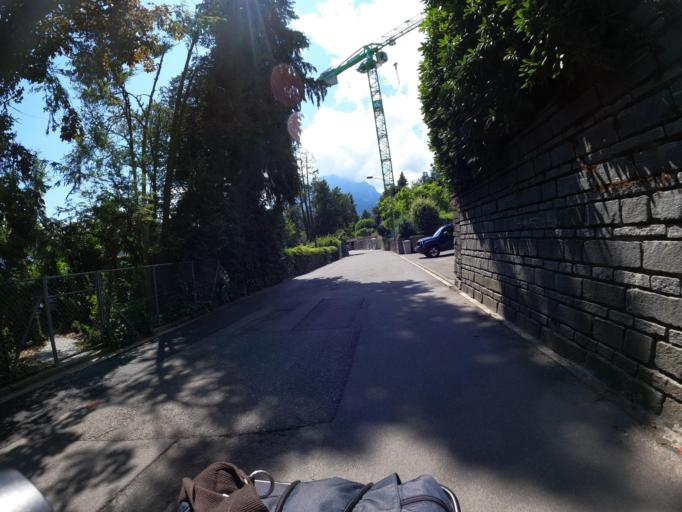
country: CH
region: Nidwalden
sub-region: Nidwalden
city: Stansstad
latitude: 47.0038
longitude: 8.3356
